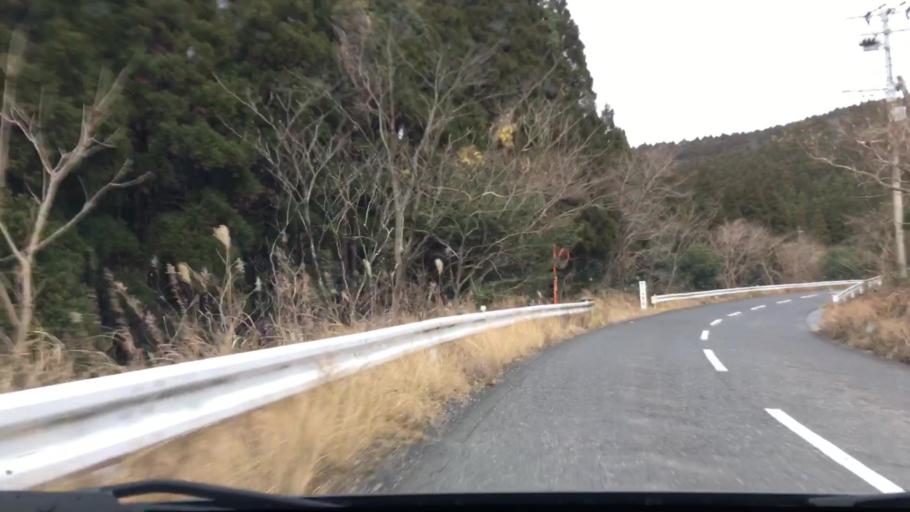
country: JP
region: Miyazaki
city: Nichinan
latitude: 31.6665
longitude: 131.3180
